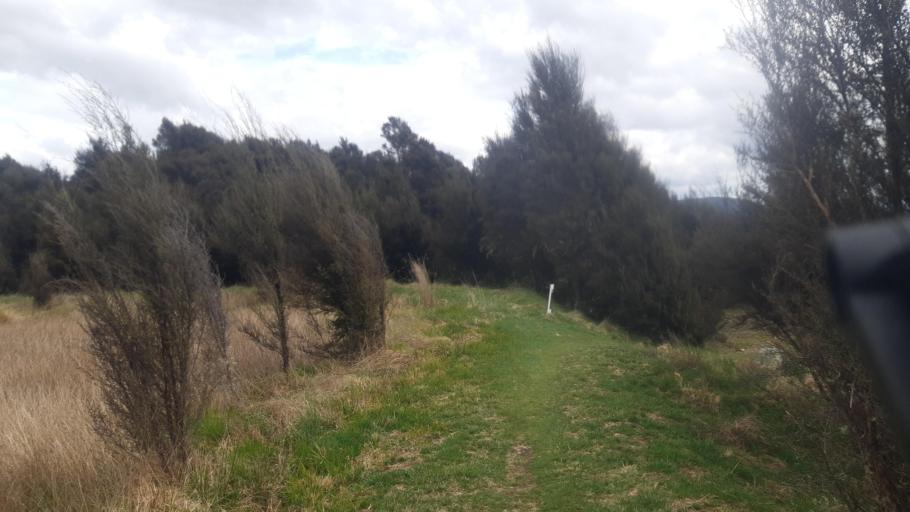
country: NZ
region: Tasman
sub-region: Tasman District
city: Wakefield
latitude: -41.7741
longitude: 172.8049
